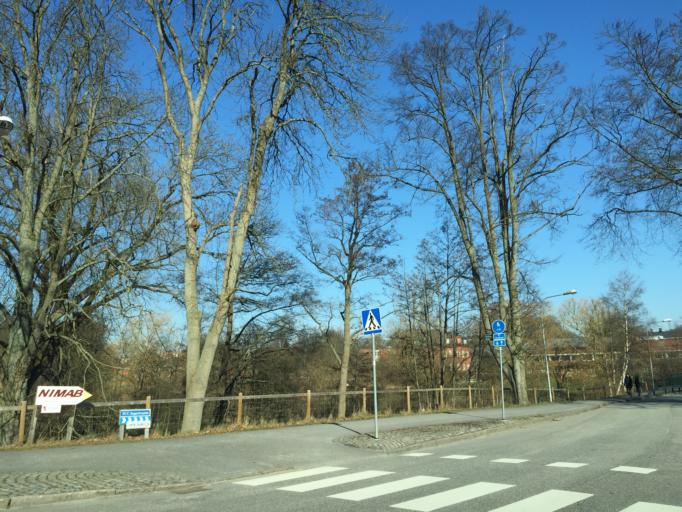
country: SE
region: Skane
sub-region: Lunds Kommun
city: Lund
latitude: 55.6839
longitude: 13.1781
